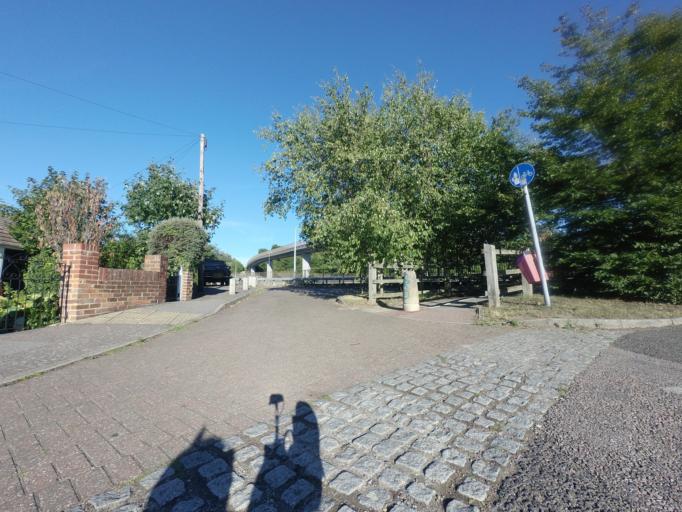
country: GB
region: England
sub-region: Kent
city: Herne Bay
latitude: 51.3603
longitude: 1.1323
